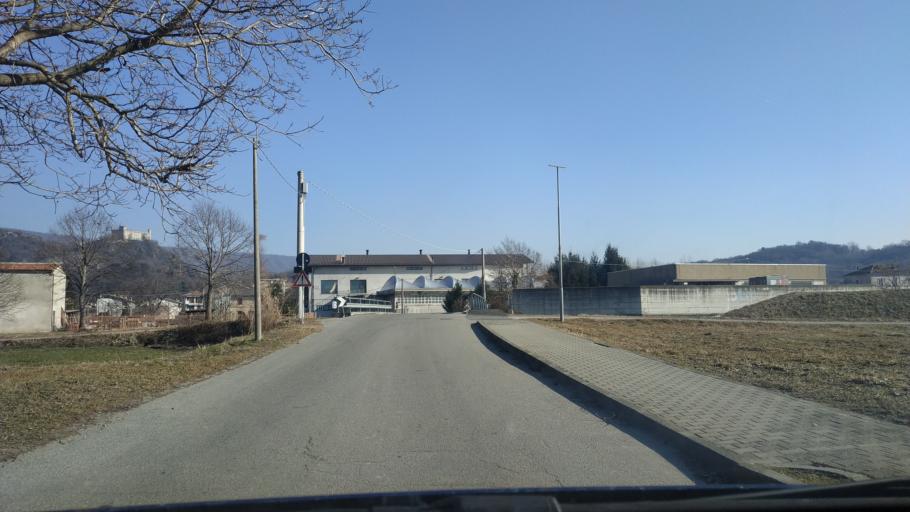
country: IT
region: Piedmont
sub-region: Provincia di Torino
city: Montalto Dora
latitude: 45.4911
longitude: 7.8566
